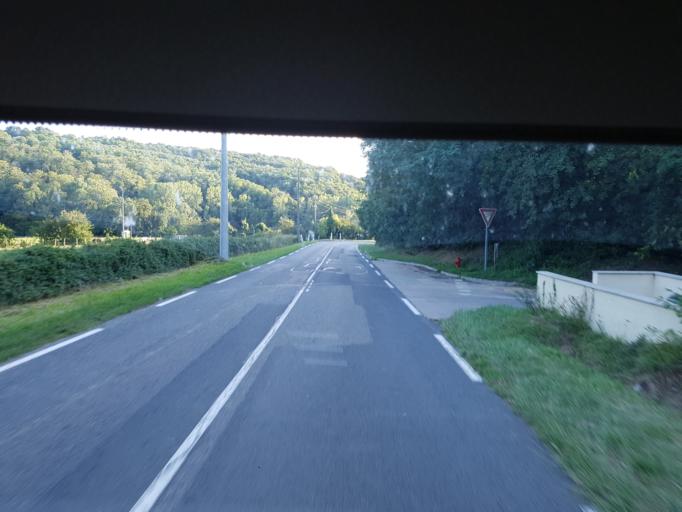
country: FR
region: Rhone-Alpes
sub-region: Departement du Rhone
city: Montanay
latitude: 45.8910
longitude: 4.8598
